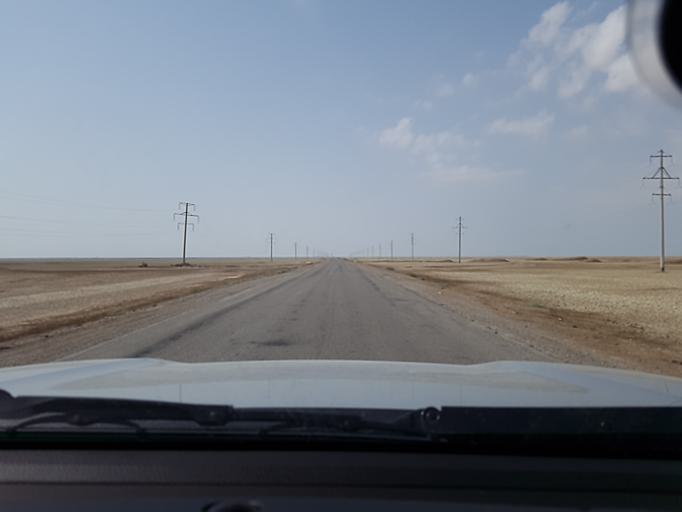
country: TM
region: Balkan
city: Gumdag
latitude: 39.0764
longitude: 54.5844
